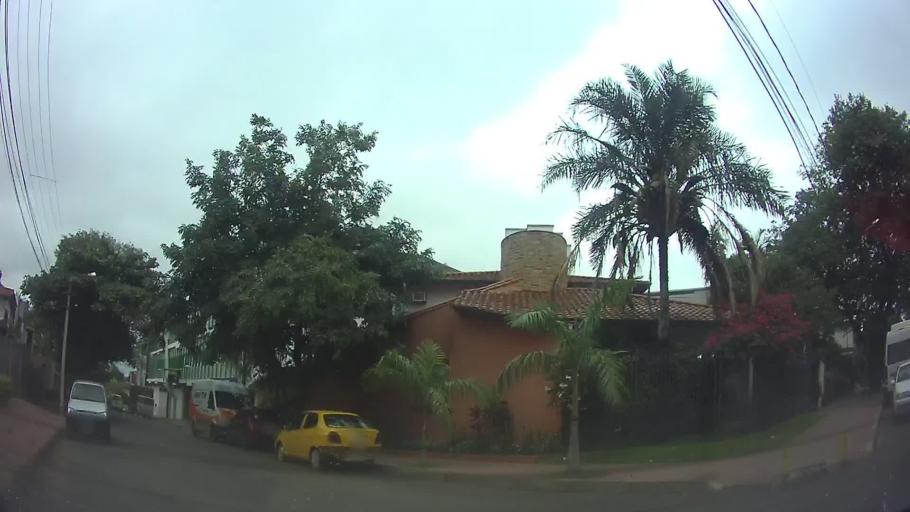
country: PY
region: Asuncion
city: Asuncion
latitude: -25.3176
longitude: -57.6189
